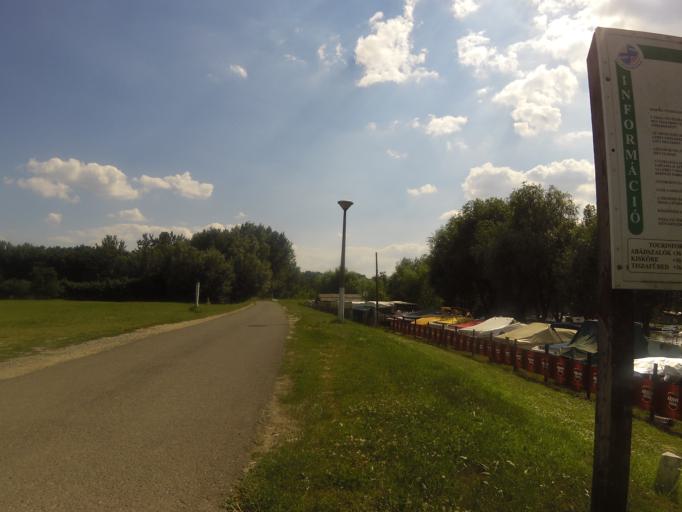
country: HU
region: Jasz-Nagykun-Szolnok
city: Tiszafured
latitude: 47.6240
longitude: 20.7323
